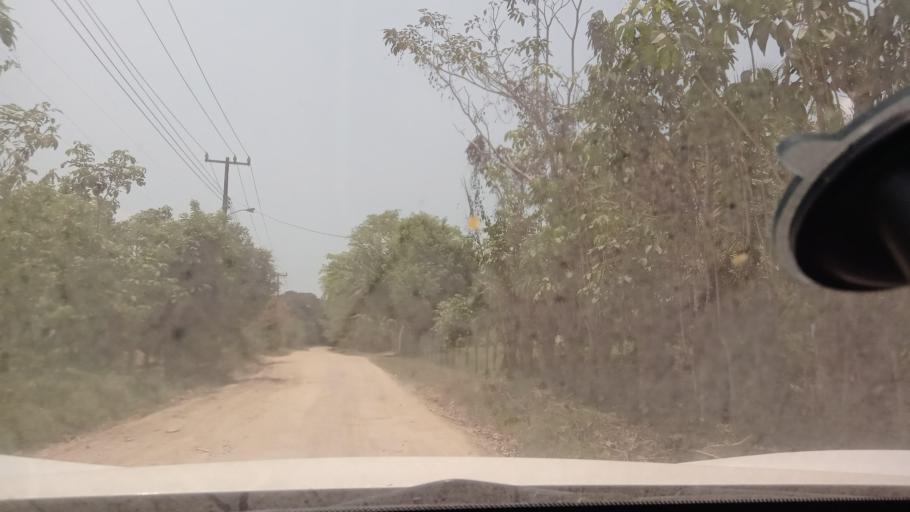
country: MX
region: Chiapas
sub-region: Tecpatan
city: Raudales Malpaso
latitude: 17.4558
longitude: -93.7962
